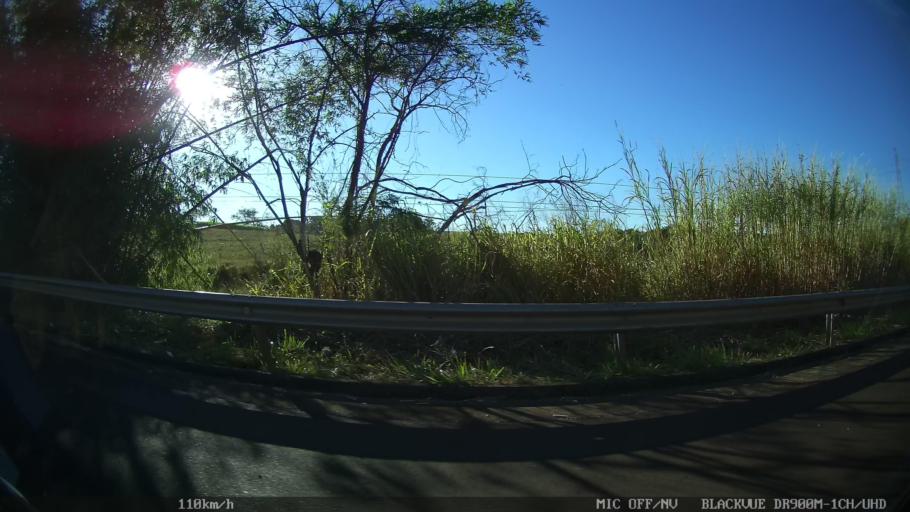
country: BR
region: Sao Paulo
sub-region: Olimpia
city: Olimpia
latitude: -20.7080
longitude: -48.9653
